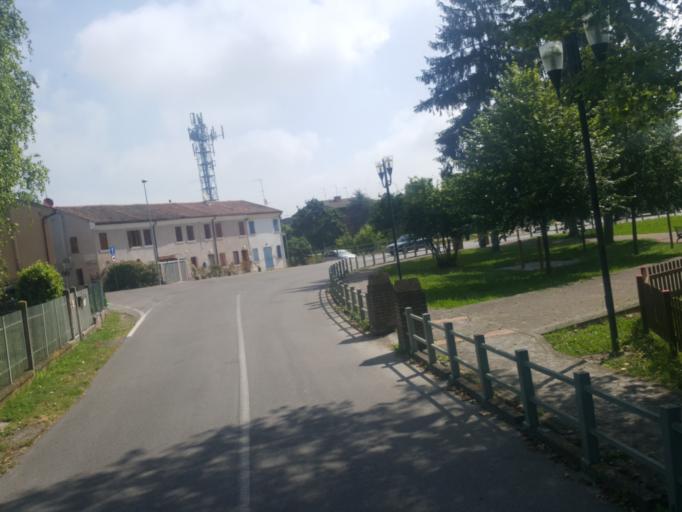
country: IT
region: Veneto
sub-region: Provincia di Rovigo
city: Canaro
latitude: 44.9358
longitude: 11.6758
